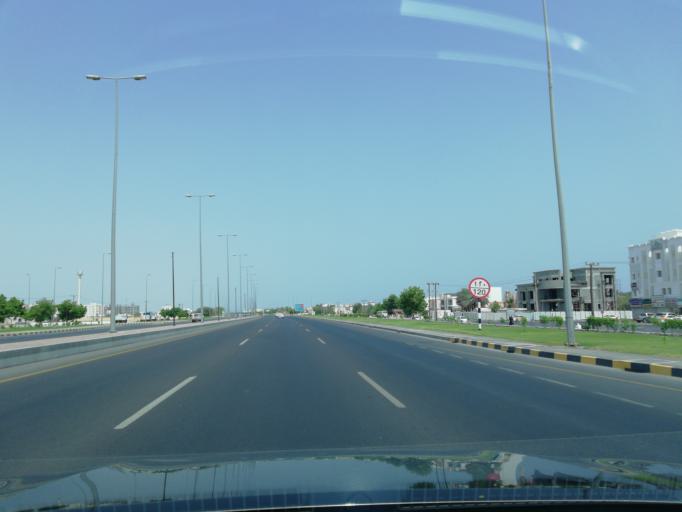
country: OM
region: Muhafazat Masqat
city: As Sib al Jadidah
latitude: 23.6761
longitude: 58.1348
